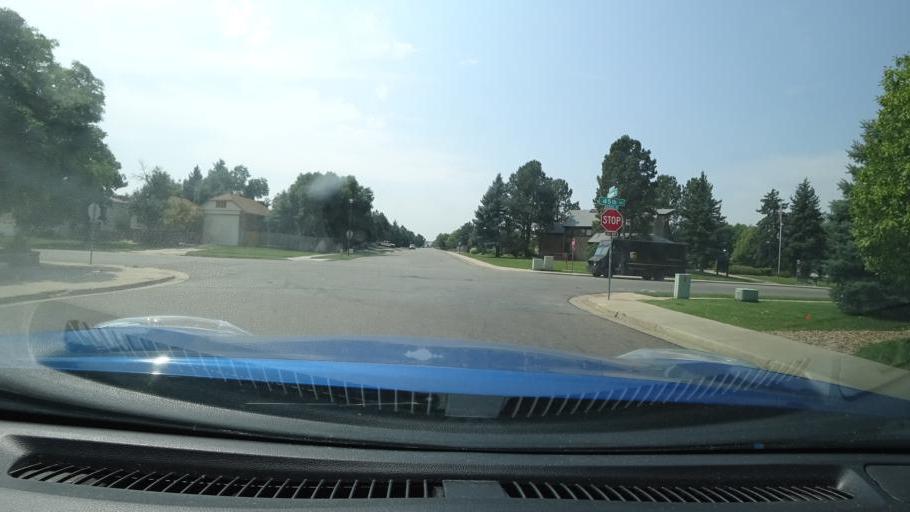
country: US
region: Colorado
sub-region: Adams County
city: Aurora
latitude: 39.7782
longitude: -104.7691
